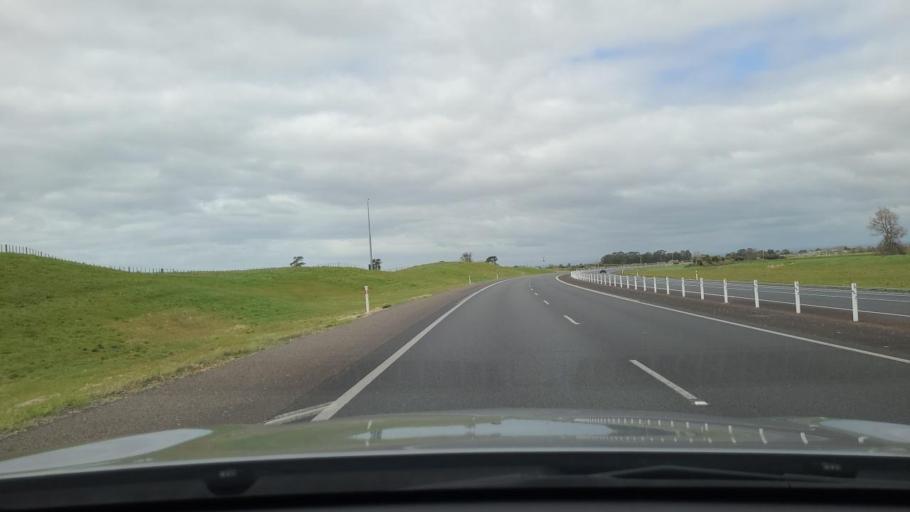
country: NZ
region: Bay of Plenty
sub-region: Western Bay of Plenty District
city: Maketu
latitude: -37.7336
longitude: 176.3465
